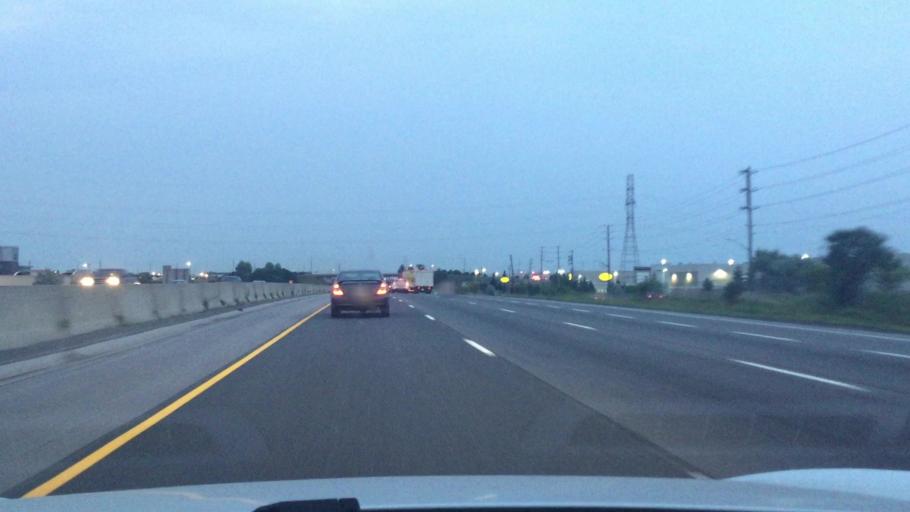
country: CA
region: Ontario
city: Oshawa
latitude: 43.8669
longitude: -78.9135
